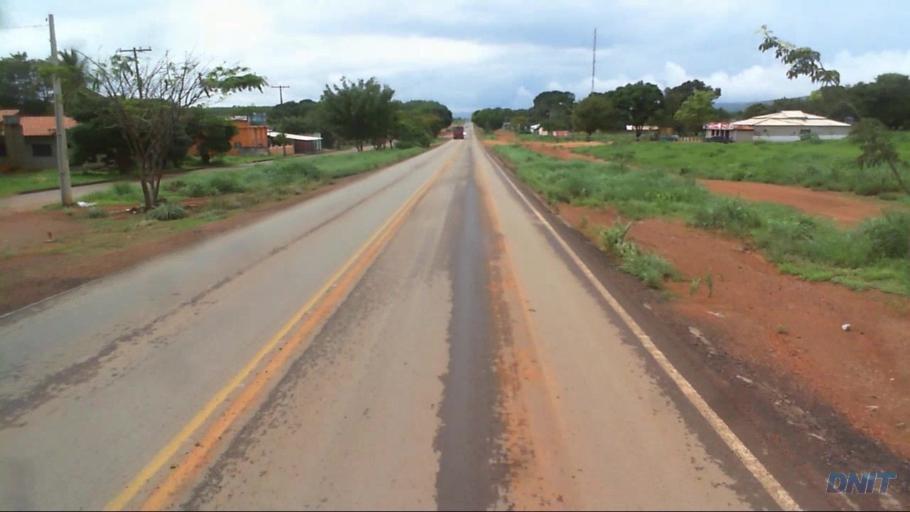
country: BR
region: Goias
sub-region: Padre Bernardo
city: Padre Bernardo
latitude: -15.2605
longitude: -48.2656
